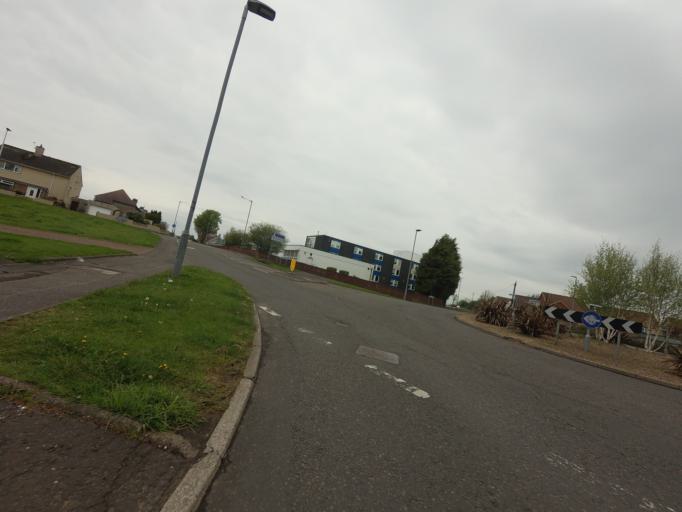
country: GB
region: Scotland
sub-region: Falkirk
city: Polmont
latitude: 55.9824
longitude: -3.7254
